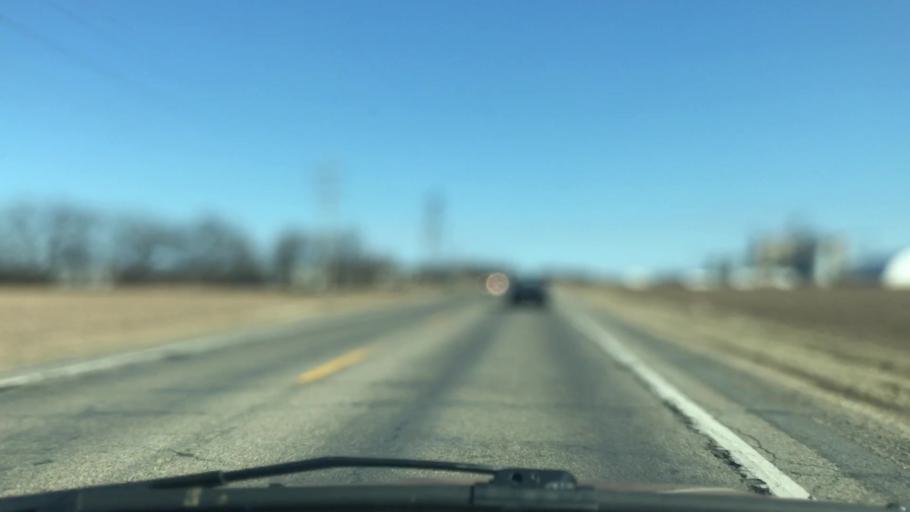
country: US
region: Indiana
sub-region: Porter County
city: Kouts
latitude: 41.3675
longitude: -87.0270
